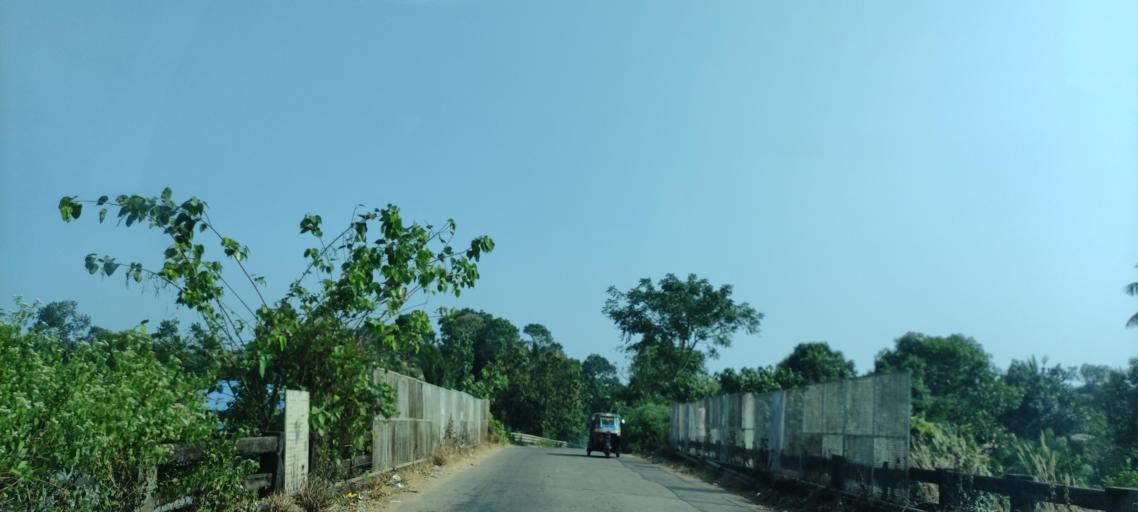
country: IN
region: Kerala
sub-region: Kollam
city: Panmana
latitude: 9.0502
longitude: 76.5661
